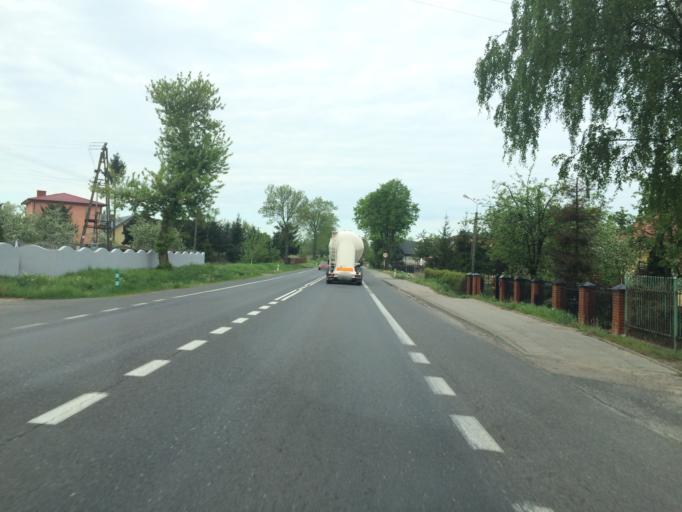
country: PL
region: Masovian Voivodeship
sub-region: Powiat mlawski
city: Mlawa
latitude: 53.0908
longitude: 20.3669
